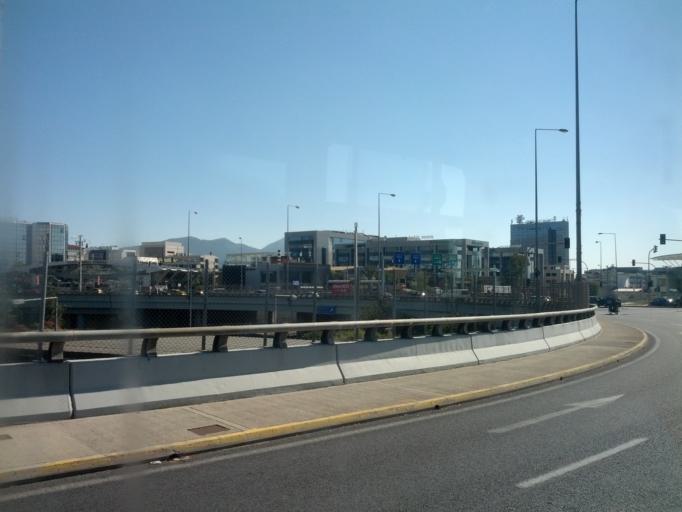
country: GR
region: Attica
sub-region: Nomarchia Athinas
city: Marousi
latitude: 38.0425
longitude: 23.8030
